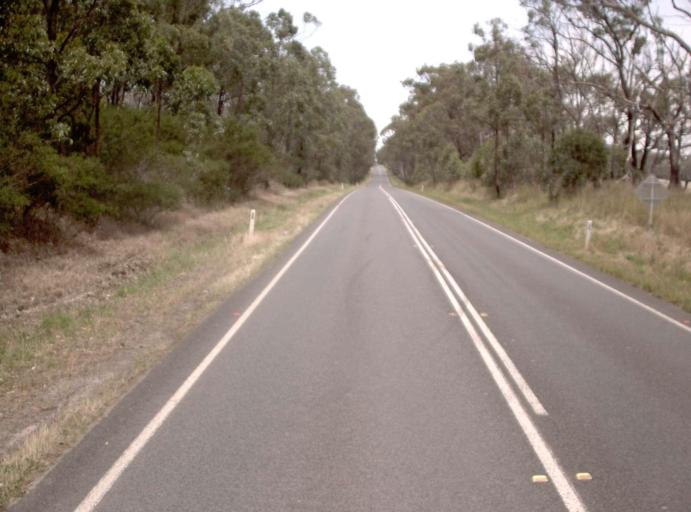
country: AU
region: Victoria
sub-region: Latrobe
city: Traralgon
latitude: -38.5161
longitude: 146.7078
